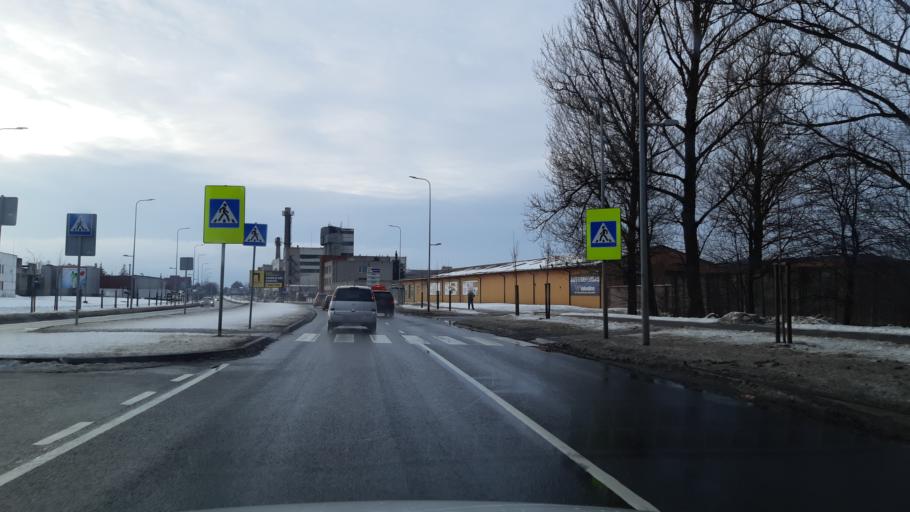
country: LT
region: Kauno apskritis
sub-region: Kaunas
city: Aleksotas
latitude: 54.8755
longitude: 23.9040
